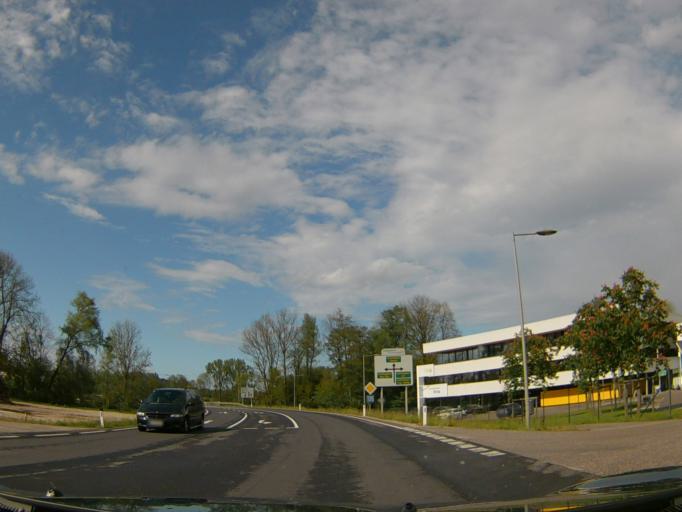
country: AT
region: Upper Austria
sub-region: Politischer Bezirk Vocklabruck
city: Schwanenstadt
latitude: 48.0504
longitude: 13.7833
